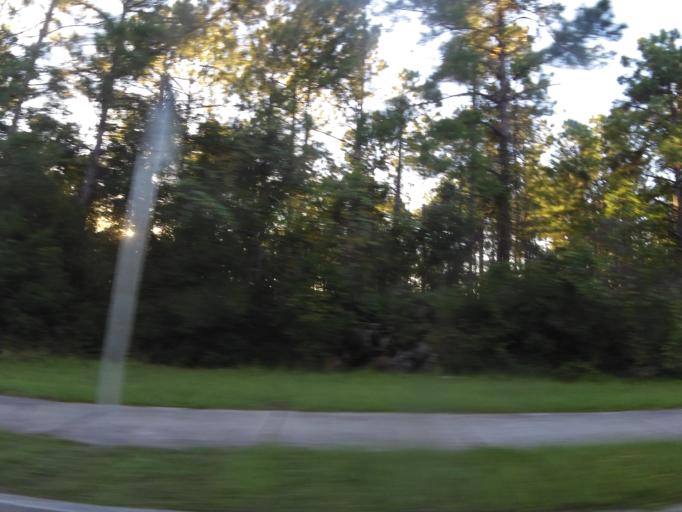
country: US
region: Florida
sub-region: Duval County
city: Jacksonville Beach
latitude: 30.2725
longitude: -81.4413
